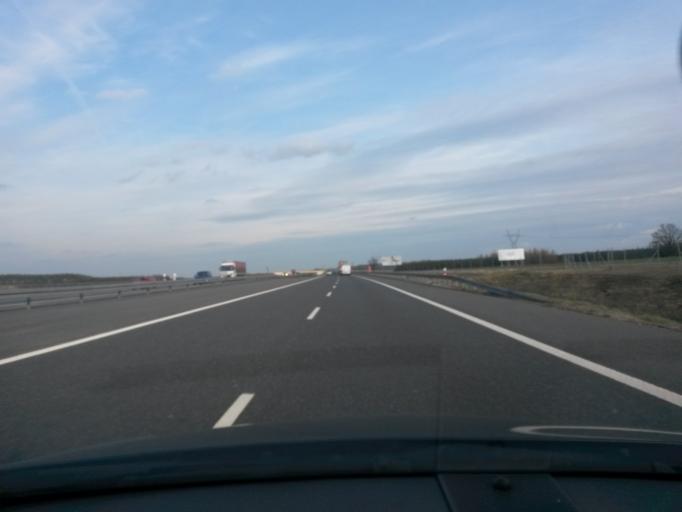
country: PL
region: Lodz Voivodeship
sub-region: Powiat zgierski
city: Ozorkow
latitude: 51.9299
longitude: 19.2910
